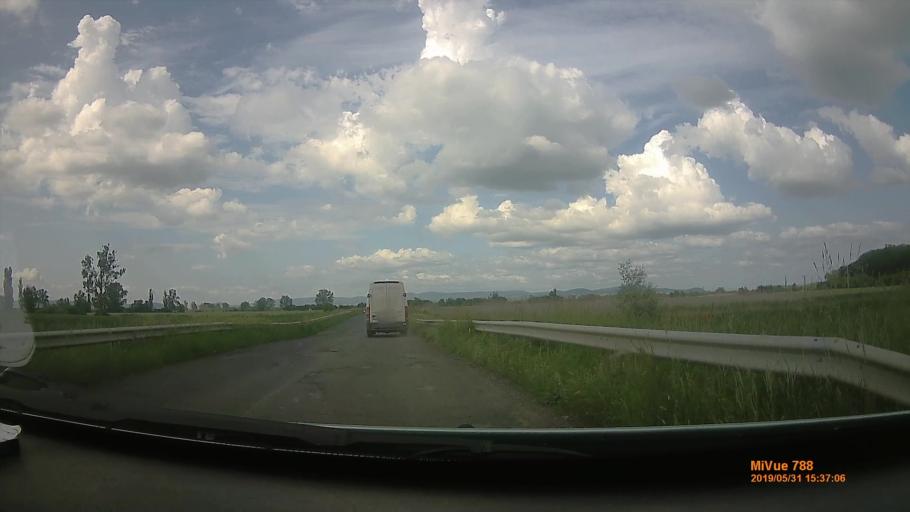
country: HU
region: Borsod-Abauj-Zemplen
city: Prugy
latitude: 48.0891
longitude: 21.2410
